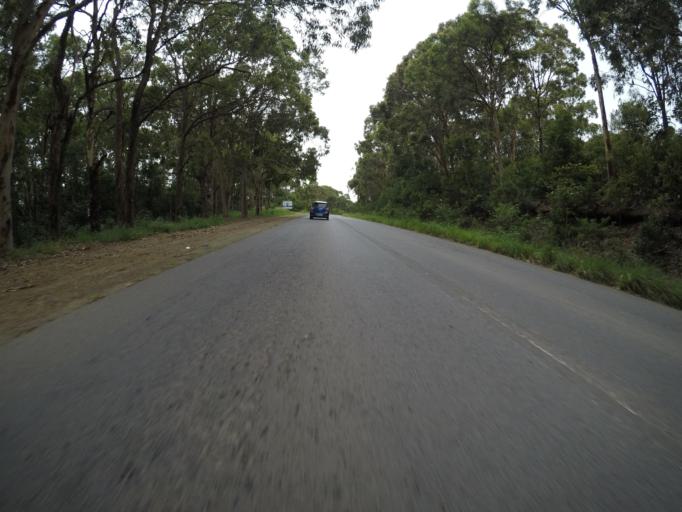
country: ZA
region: Eastern Cape
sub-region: Buffalo City Metropolitan Municipality
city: East London
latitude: -32.9370
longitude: 27.9440
